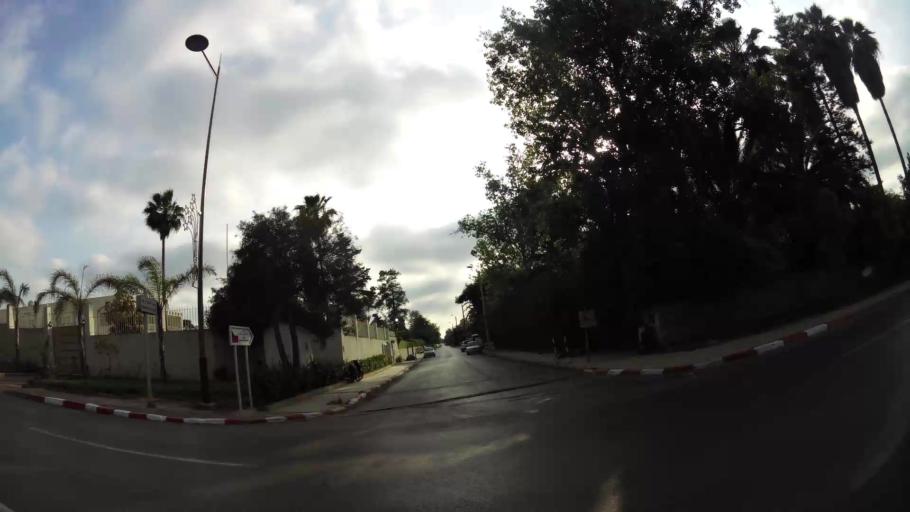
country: MA
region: Rabat-Sale-Zemmour-Zaer
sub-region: Rabat
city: Rabat
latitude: 33.9570
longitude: -6.8255
